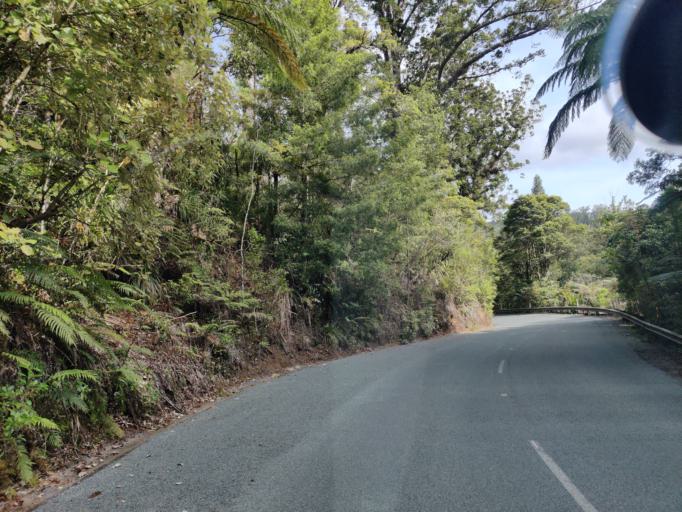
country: NZ
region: Northland
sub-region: Kaipara District
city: Dargaville
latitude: -35.6487
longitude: 173.5636
